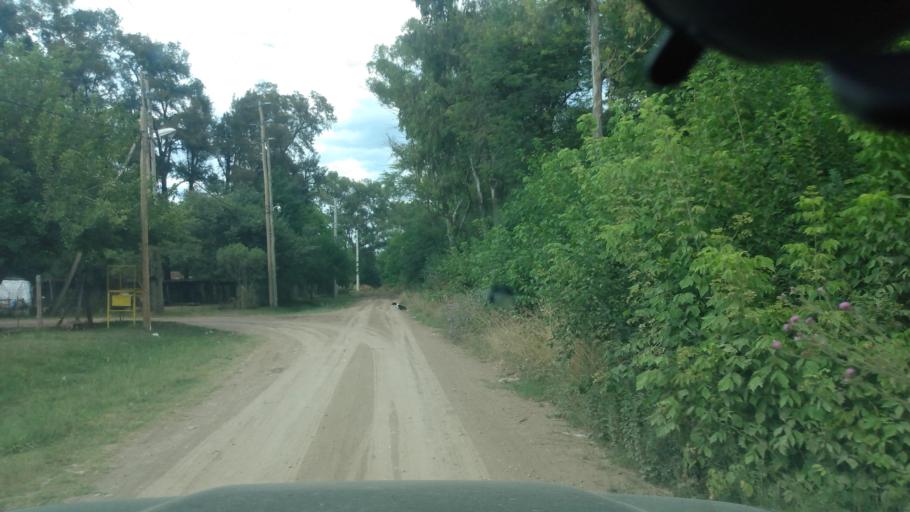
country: AR
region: Buenos Aires
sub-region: Partido de Lujan
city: Lujan
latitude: -34.5980
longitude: -59.0583
